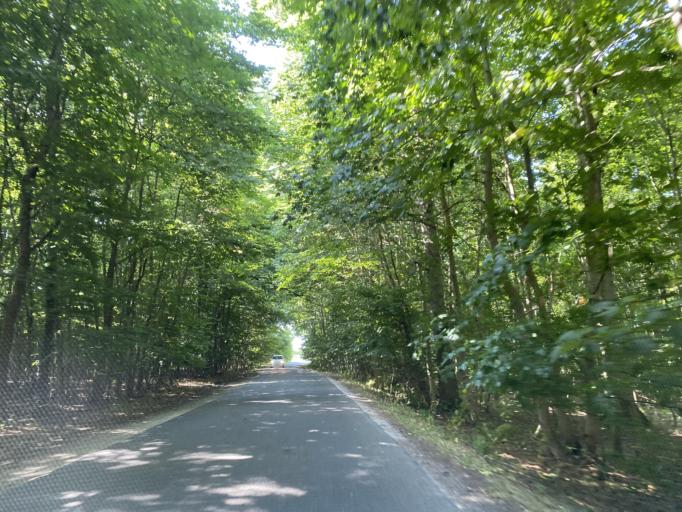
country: DK
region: Central Jutland
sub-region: Favrskov Kommune
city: Hammel
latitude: 56.2520
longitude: 9.8062
